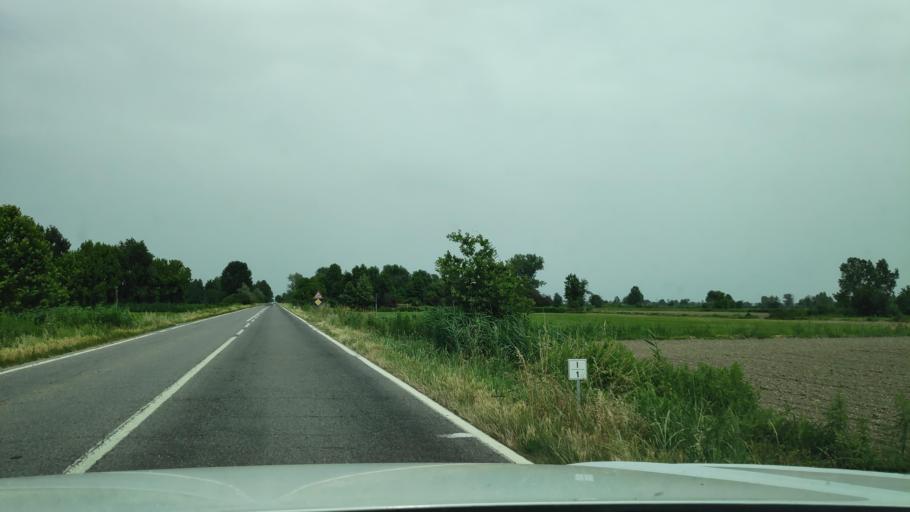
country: IT
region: Lombardy
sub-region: Provincia di Cremona
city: Cremosano
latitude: 45.4055
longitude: 9.6425
